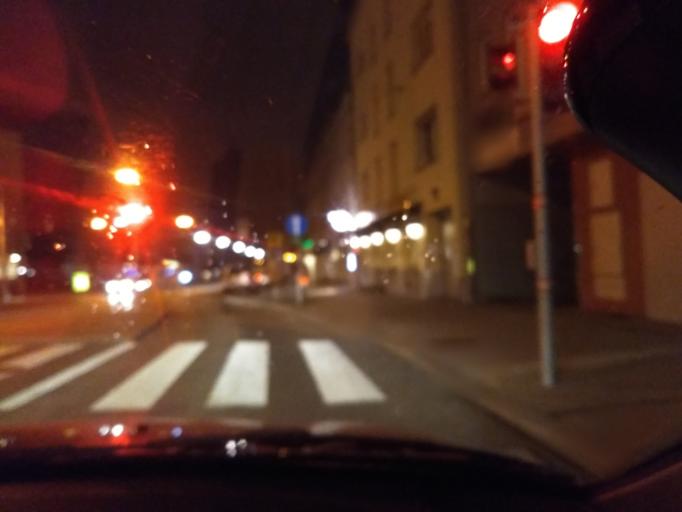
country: AT
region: Lower Austria
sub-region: Politischer Bezirk Modling
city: Perchtoldsdorf
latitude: 48.1678
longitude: 16.2838
